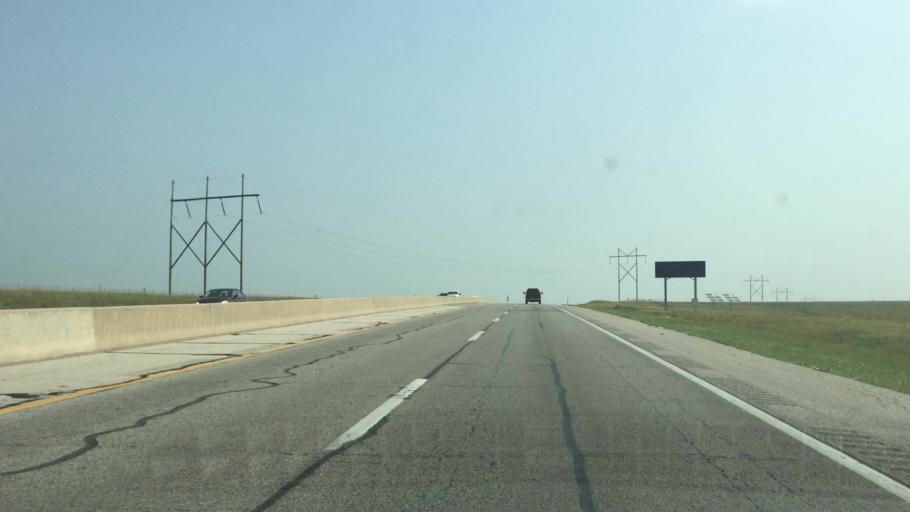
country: US
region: Kansas
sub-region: Chase County
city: Cottonwood Falls
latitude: 38.1861
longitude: -96.4563
